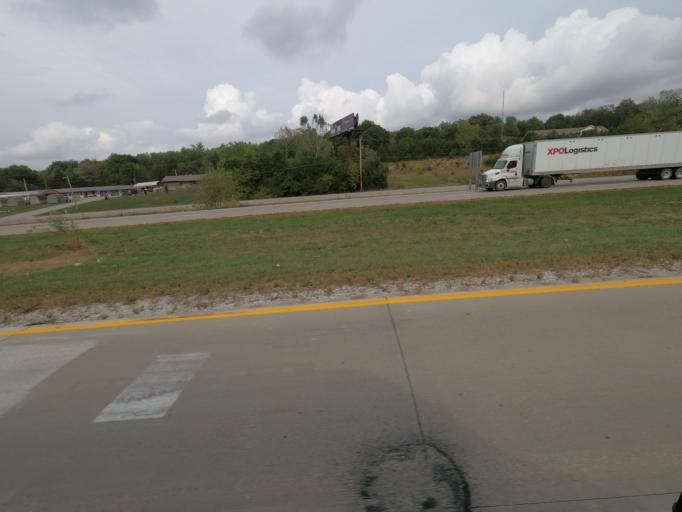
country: US
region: Iowa
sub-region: Wapello County
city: Ottumwa
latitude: 41.0062
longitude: -92.3613
